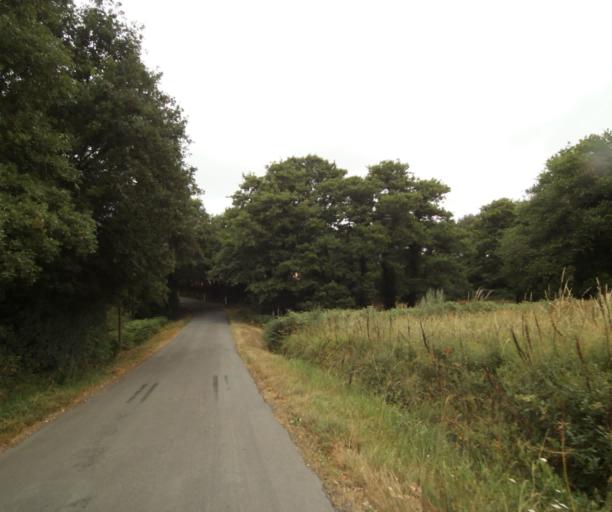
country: FR
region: Pays de la Loire
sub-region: Departement de la Vendee
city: Chateau-d'Olonne
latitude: 46.4820
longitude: -1.6883
